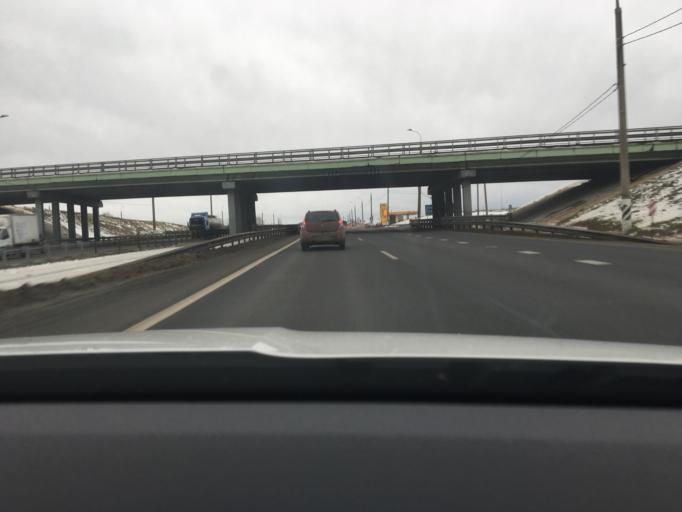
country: RU
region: Moskovskaya
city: Serpukhov
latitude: 54.8559
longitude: 37.4777
